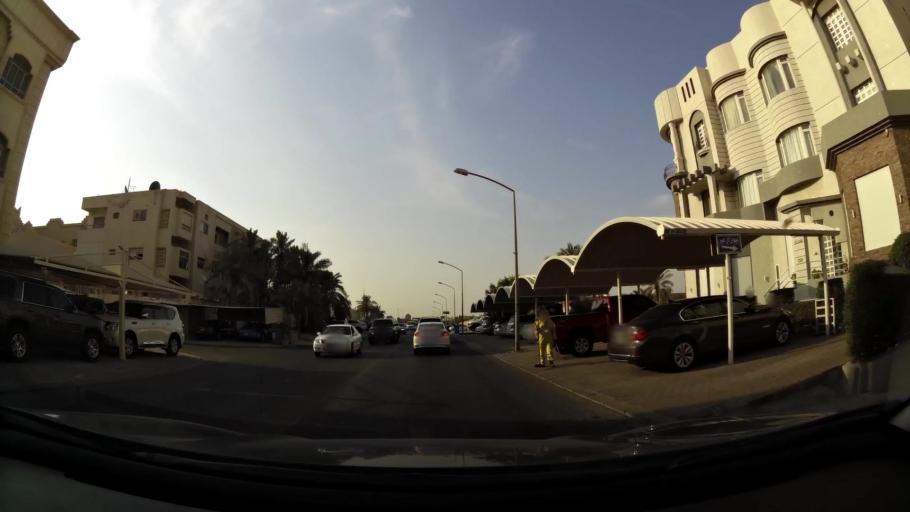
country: KW
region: Muhafazat Hawalli
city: Ar Rumaythiyah
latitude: 29.3193
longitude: 48.0768
